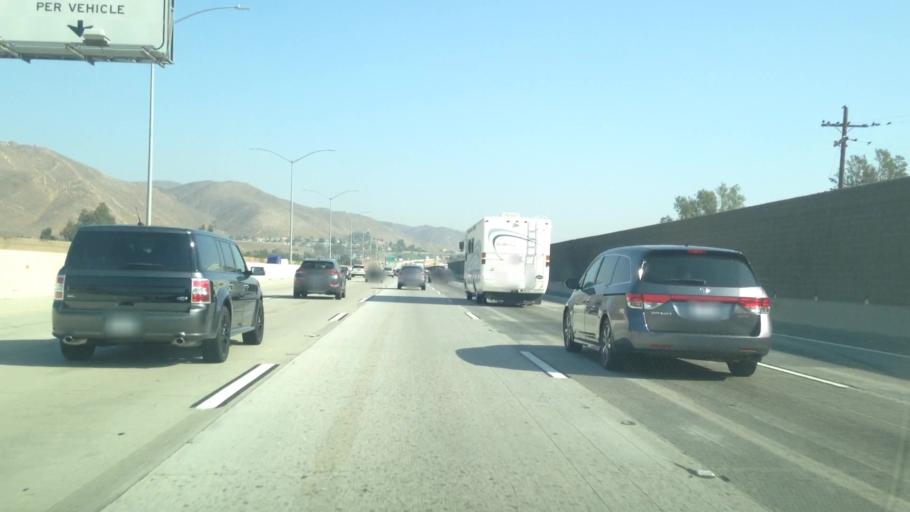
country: US
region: California
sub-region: Riverside County
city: Glen Avon
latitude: 34.0190
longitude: -117.4990
